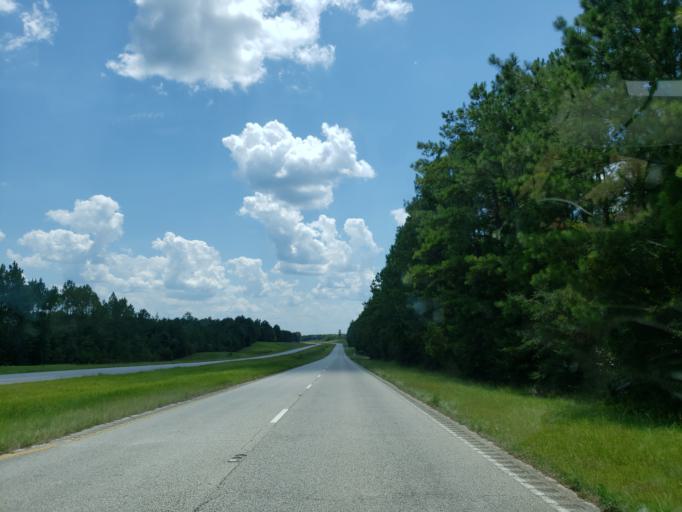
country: US
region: Mississippi
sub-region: Wayne County
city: Belmont
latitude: 31.3970
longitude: -88.4736
